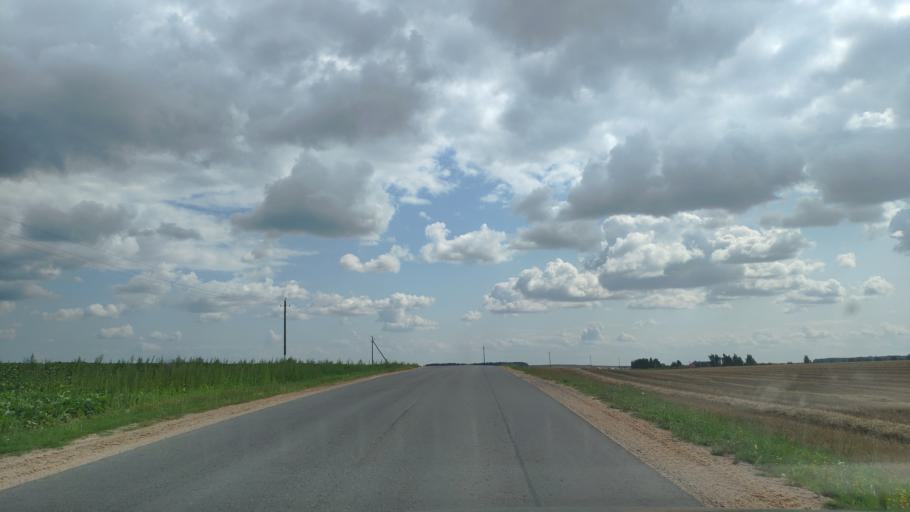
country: BY
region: Minsk
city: Khatsyezhyna
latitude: 53.8470
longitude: 27.3127
